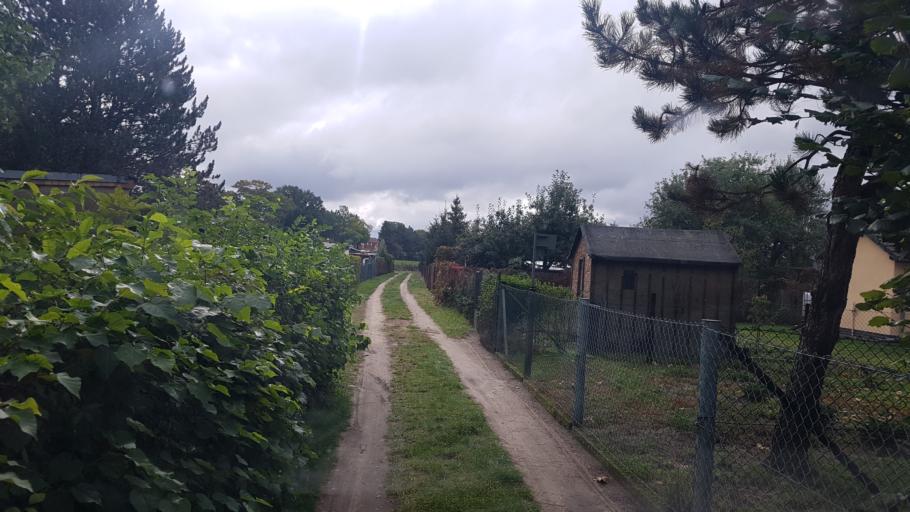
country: DE
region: Brandenburg
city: Altdobern
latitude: 51.6481
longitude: 14.0322
